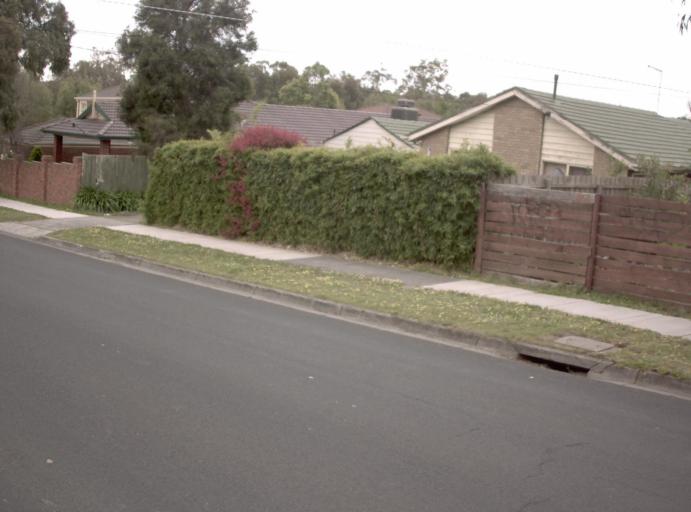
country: AU
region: Victoria
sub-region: Knox
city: Wantirna
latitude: -37.8411
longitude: 145.2274
